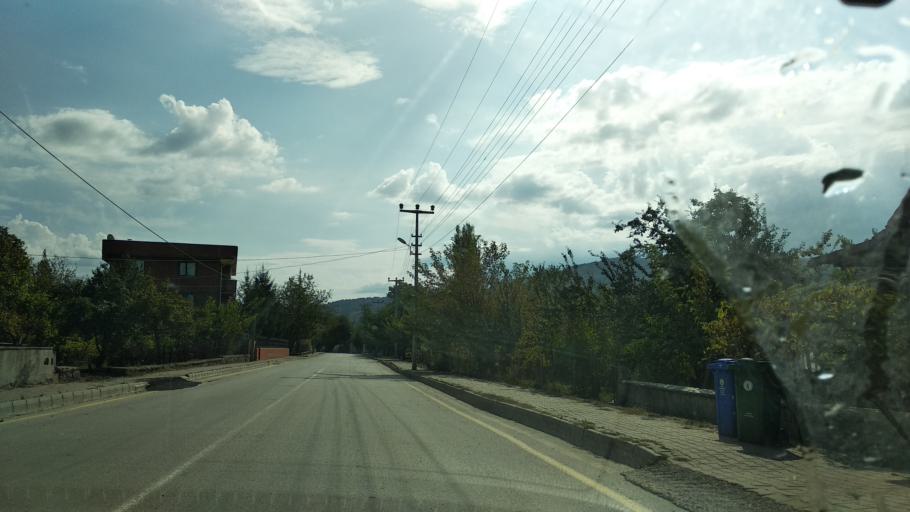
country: TR
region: Bolu
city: Seben
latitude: 40.4111
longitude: 31.5700
